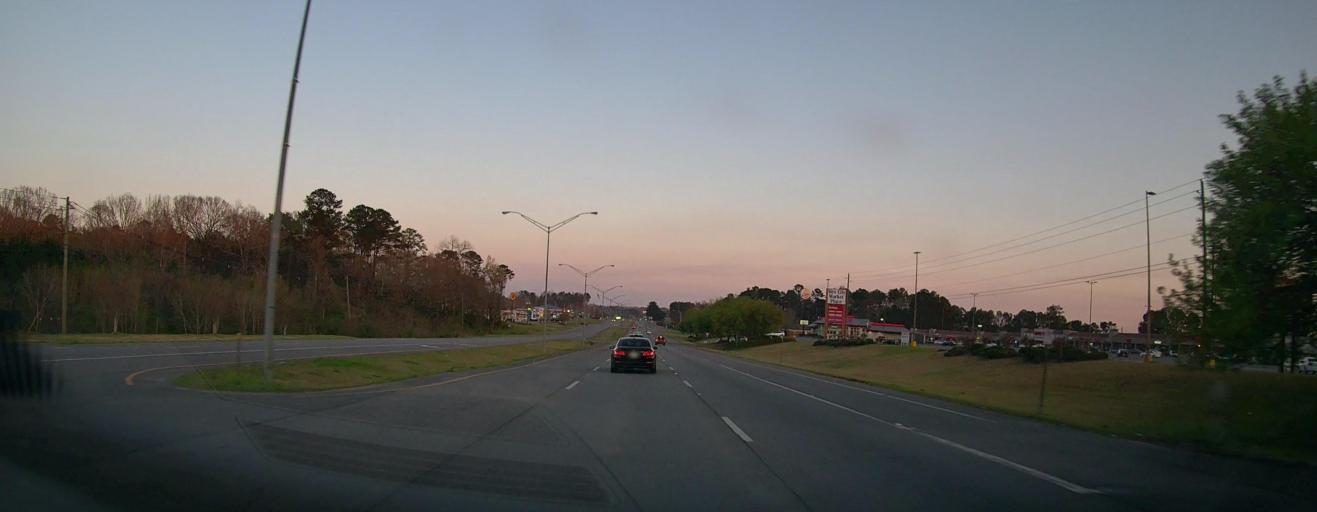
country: US
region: Alabama
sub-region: Tallapoosa County
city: Alexander City
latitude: 32.9229
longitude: -85.9599
